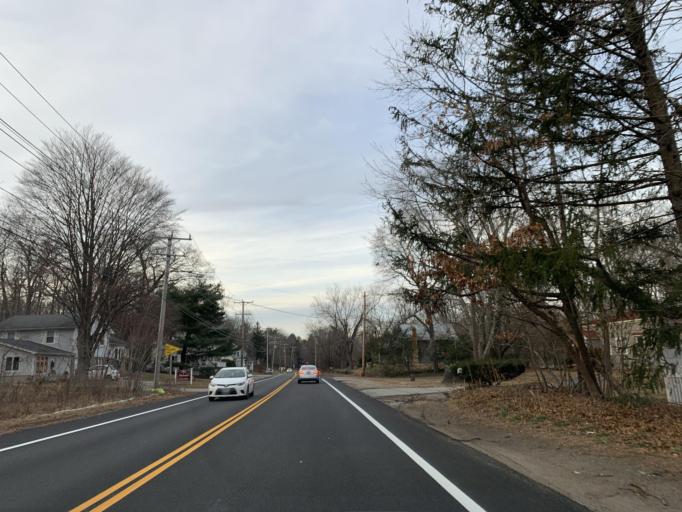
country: US
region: Rhode Island
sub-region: Providence County
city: Greenville
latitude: 41.8587
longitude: -71.5281
